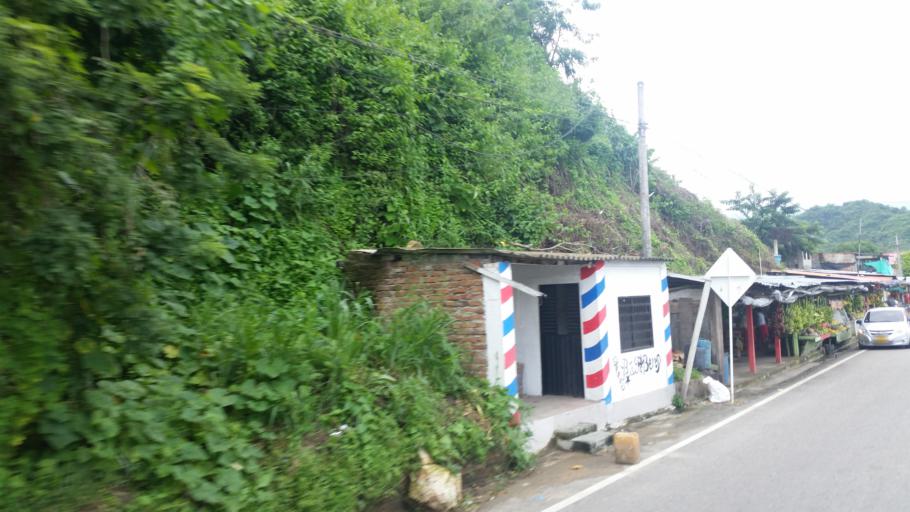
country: CO
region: Magdalena
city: Santa Marta
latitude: 11.2491
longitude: -73.8280
